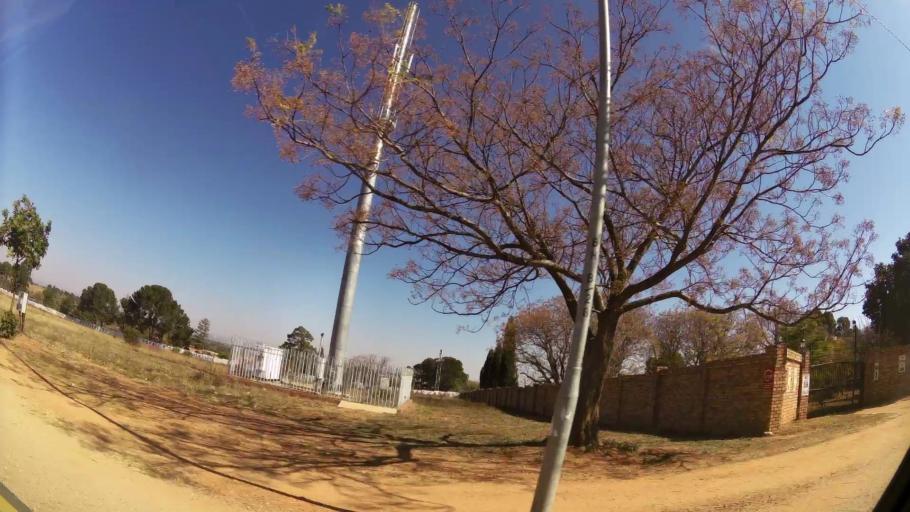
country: ZA
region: Gauteng
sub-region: City of Johannesburg Metropolitan Municipality
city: Midrand
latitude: -25.9450
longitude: 28.0972
